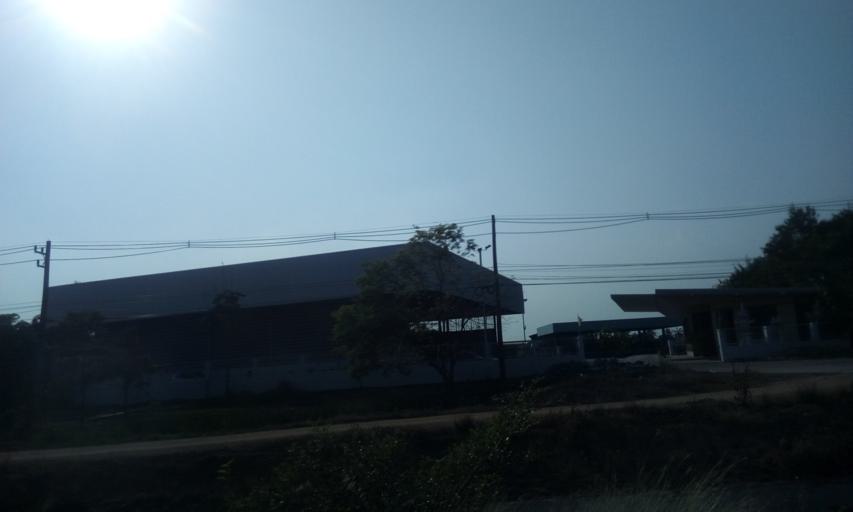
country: TH
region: Sing Buri
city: Phrom Buri
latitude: 14.8368
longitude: 100.4345
